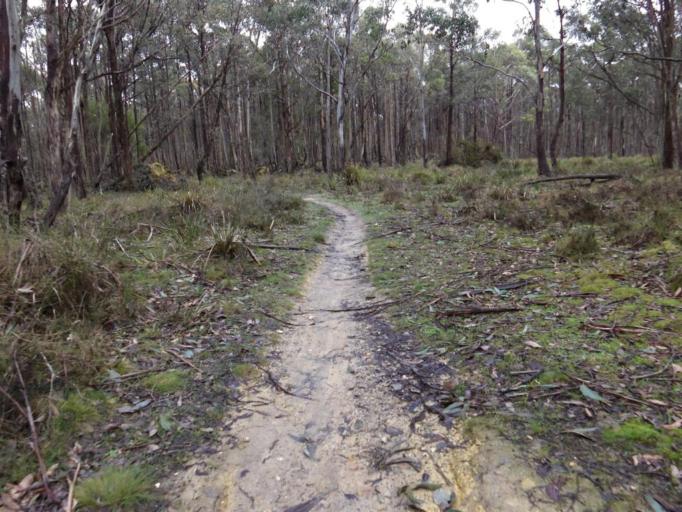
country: AU
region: Victoria
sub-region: Moorabool
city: Bacchus Marsh
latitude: -37.4065
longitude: 144.4886
